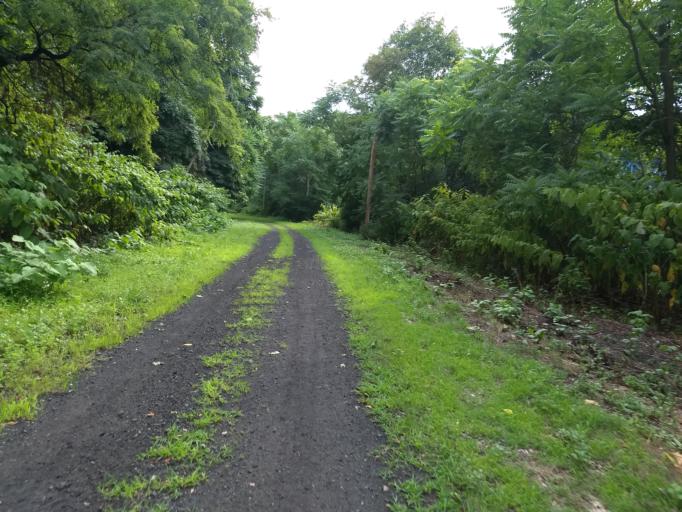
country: US
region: Pennsylvania
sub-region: Armstrong County
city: Freeport
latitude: 40.6680
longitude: -79.6895
